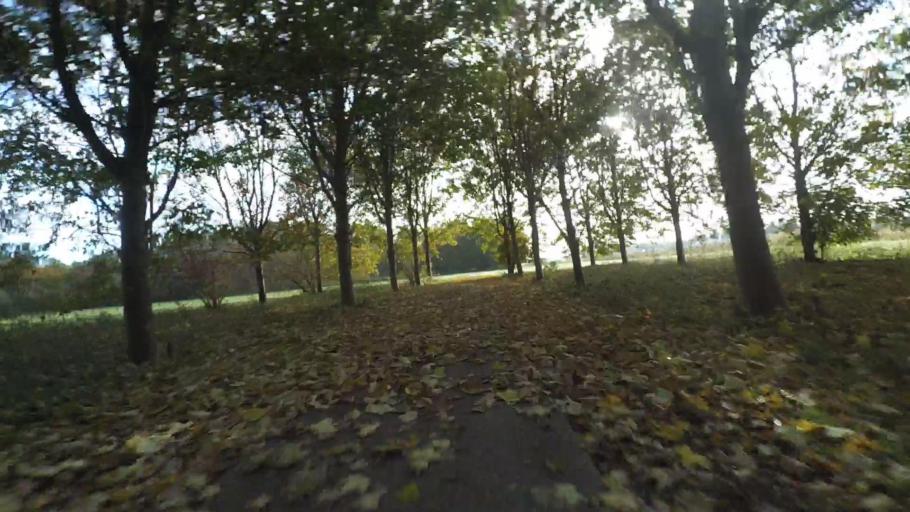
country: NL
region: Utrecht
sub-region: Gemeente Bunschoten
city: Spakenburg
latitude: 52.3182
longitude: 5.3259
